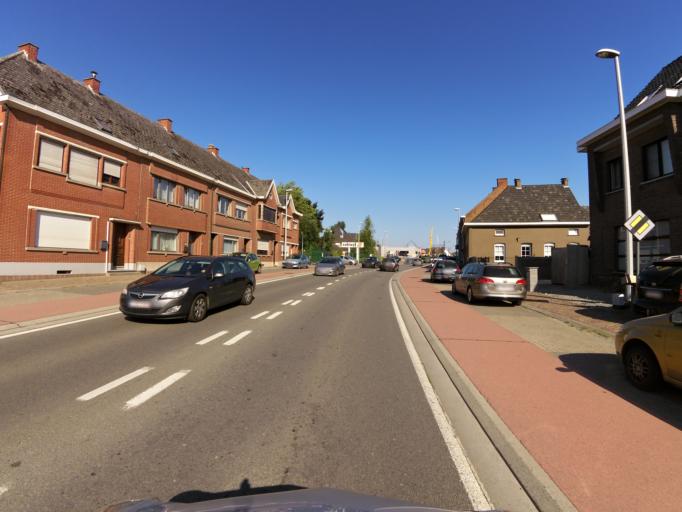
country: BE
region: Wallonia
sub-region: Province du Hainaut
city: Flobecq
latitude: 50.7972
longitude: 3.7605
